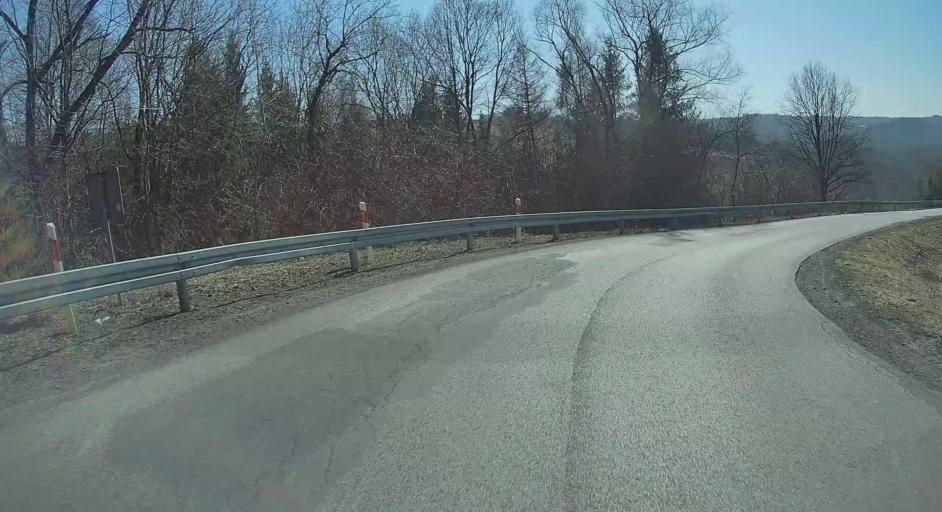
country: PL
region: Subcarpathian Voivodeship
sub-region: Powiat rzeszowski
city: Dynow
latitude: 49.7259
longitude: 22.2987
